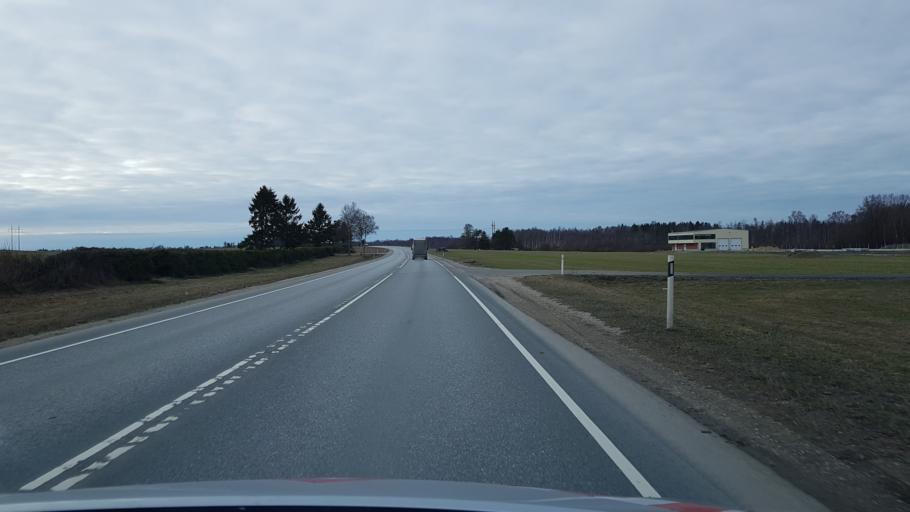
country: EE
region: Laeaene-Virumaa
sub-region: Someru vald
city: Someru
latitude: 59.3694
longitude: 26.4296
